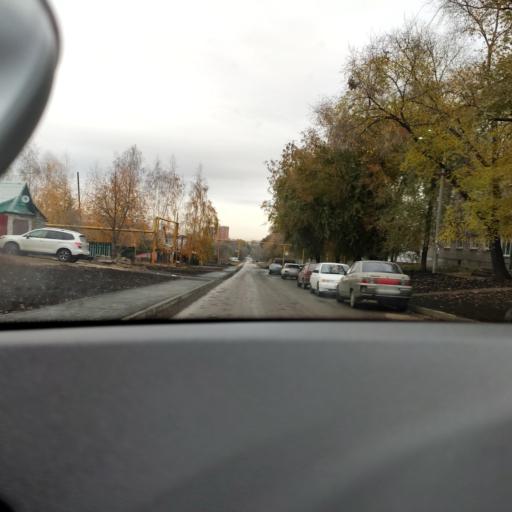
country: RU
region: Samara
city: Samara
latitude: 53.2205
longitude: 50.2224
